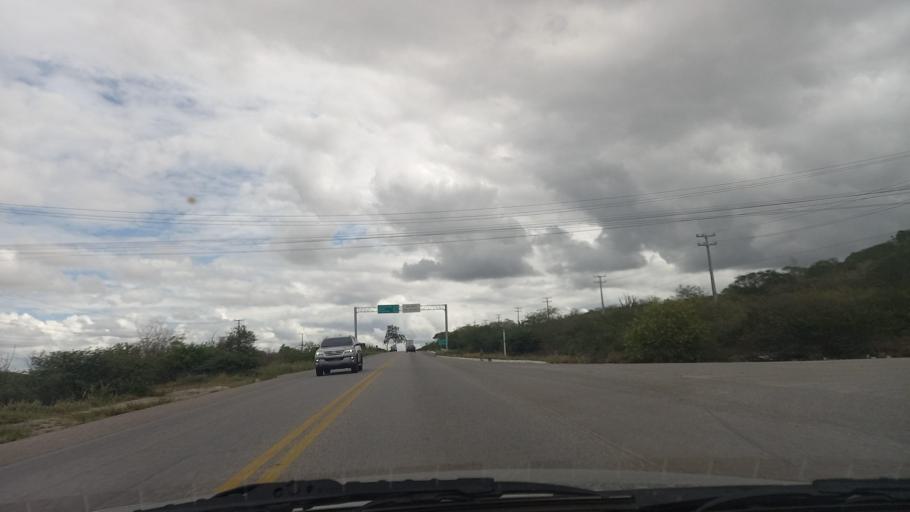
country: BR
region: Pernambuco
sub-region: Cachoeirinha
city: Cachoeirinha
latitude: -8.3319
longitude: -36.1492
